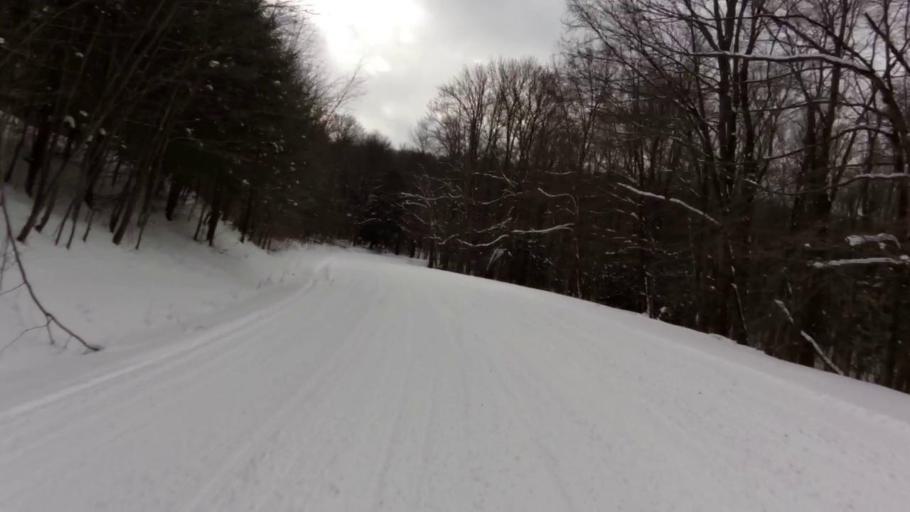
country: US
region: New York
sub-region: Cattaraugus County
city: Salamanca
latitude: 42.0377
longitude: -78.7870
